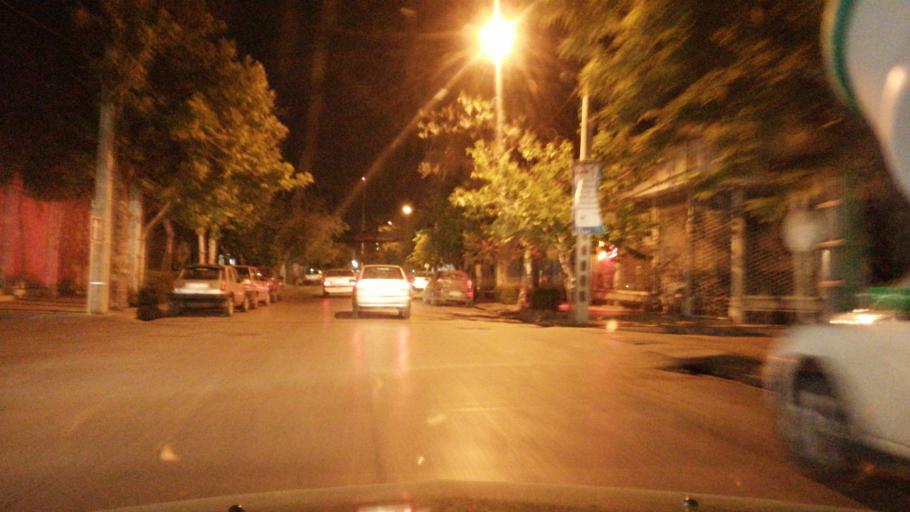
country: IR
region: Razavi Khorasan
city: Mashhad
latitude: 36.3044
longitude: 59.6005
